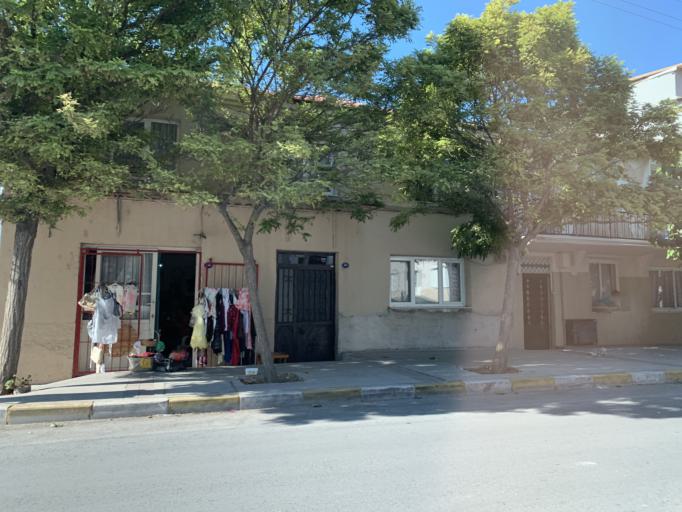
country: TR
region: Izmir
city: Urla
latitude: 38.3212
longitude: 26.7597
